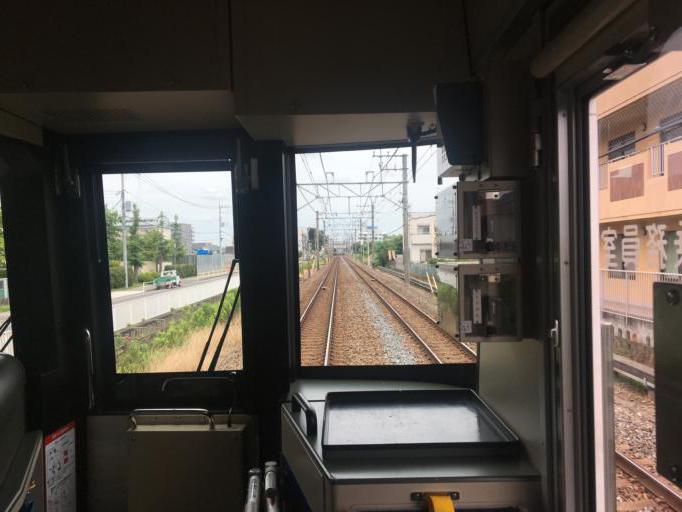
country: JP
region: Saitama
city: Kasukabe
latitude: 35.9445
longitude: 139.7720
